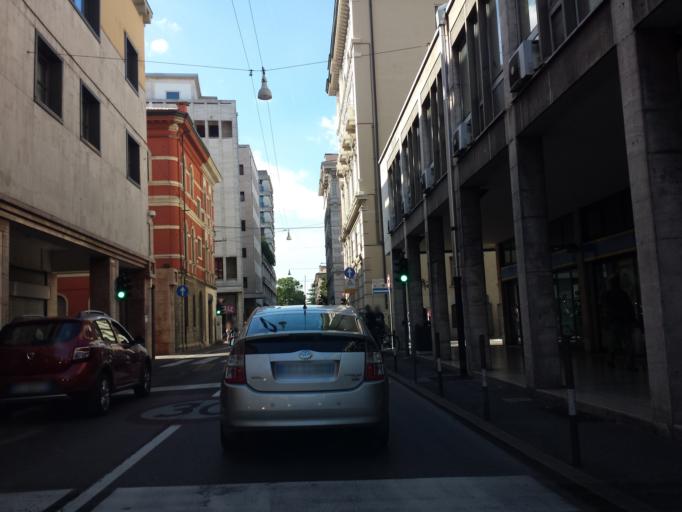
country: IT
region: Veneto
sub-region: Provincia di Padova
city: Padova
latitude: 45.4160
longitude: 11.8801
